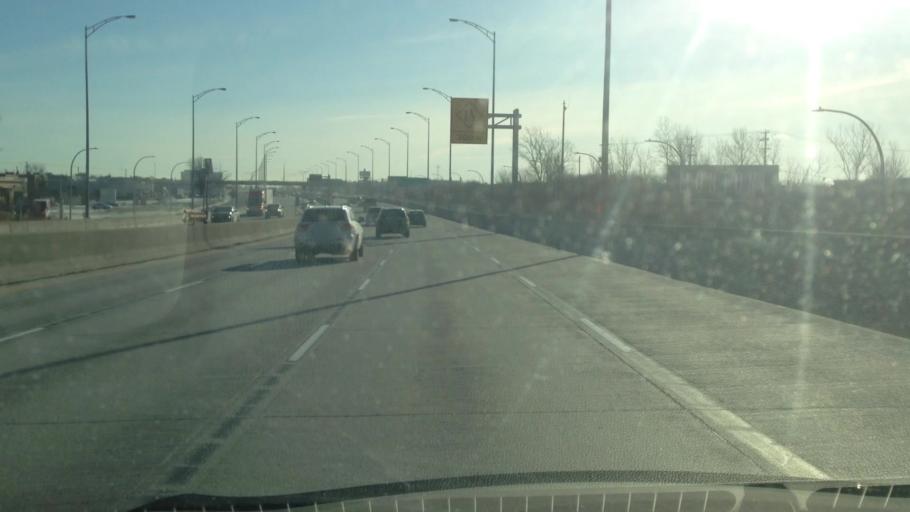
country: CA
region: Quebec
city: Dorval
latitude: 45.5025
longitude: -73.7558
